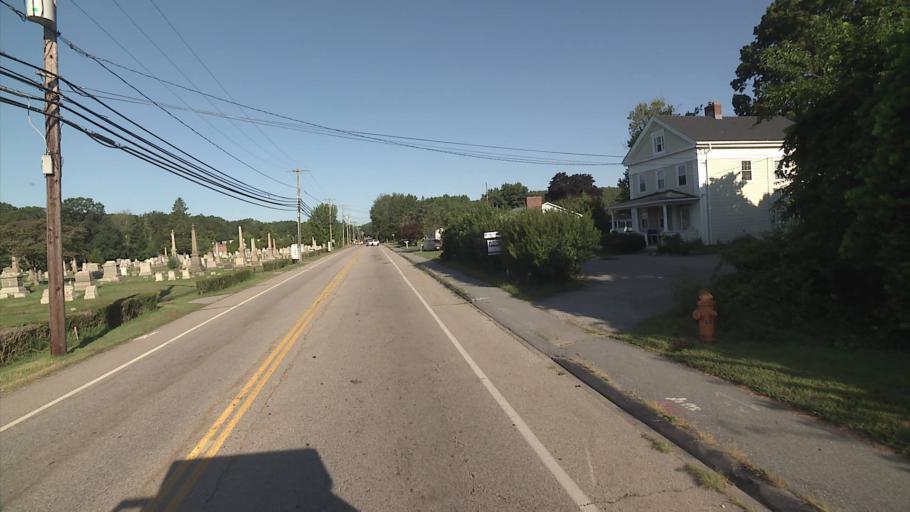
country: US
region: Connecticut
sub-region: New London County
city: Central Waterford
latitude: 41.3468
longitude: -72.1411
